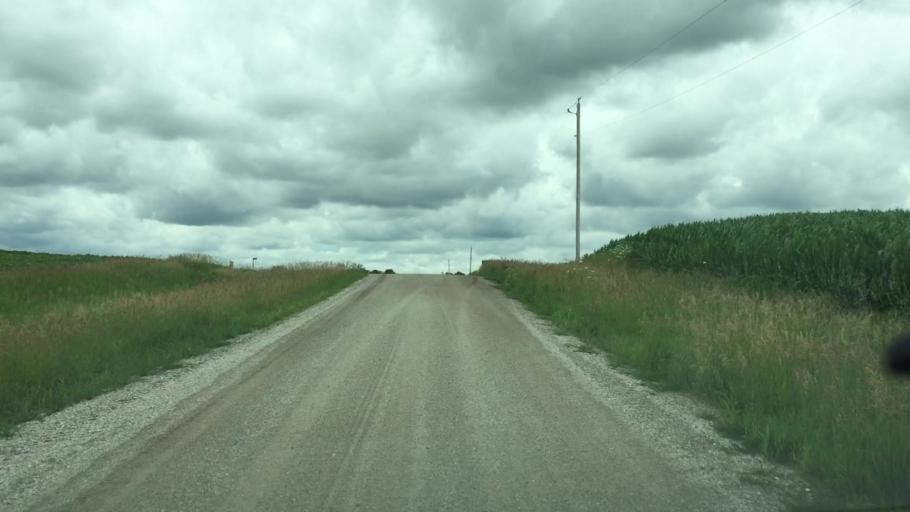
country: US
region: Iowa
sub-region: Jasper County
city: Monroe
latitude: 41.6010
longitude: -93.1360
